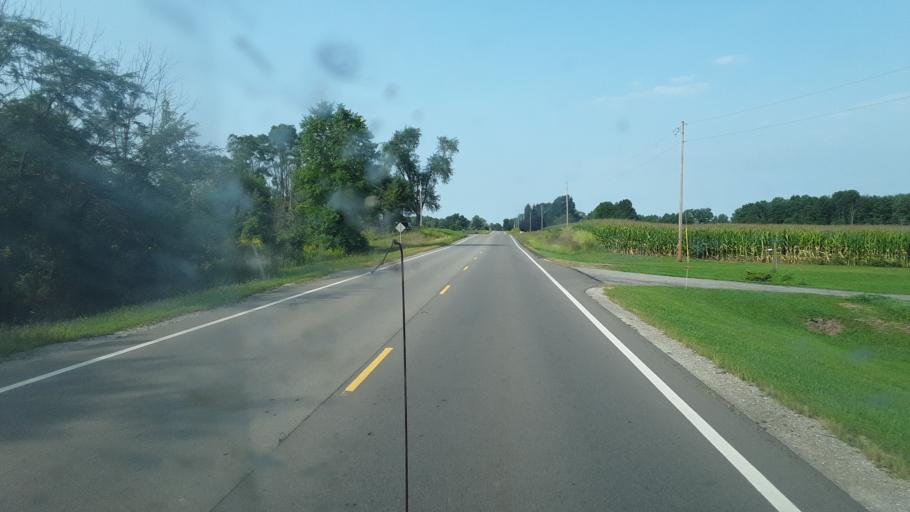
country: US
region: Ohio
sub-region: Morrow County
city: Mount Gilead
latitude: 40.6440
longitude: -82.9190
